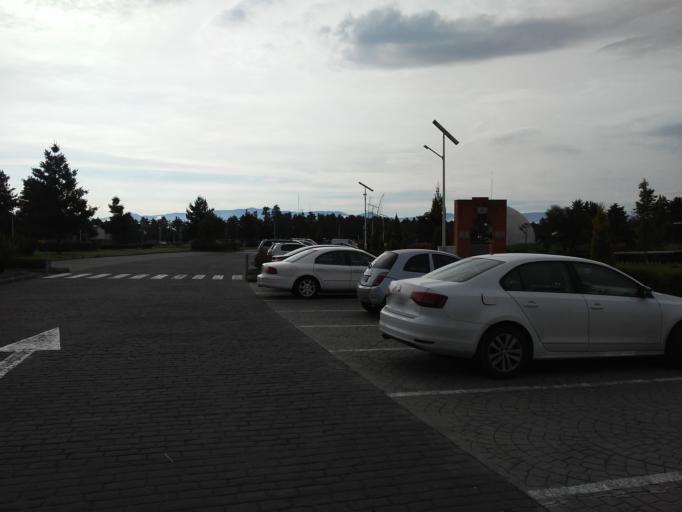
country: MX
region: Mexico
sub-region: Metepec
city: San Salvador Tizatlalli
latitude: 19.2480
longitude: -99.5862
